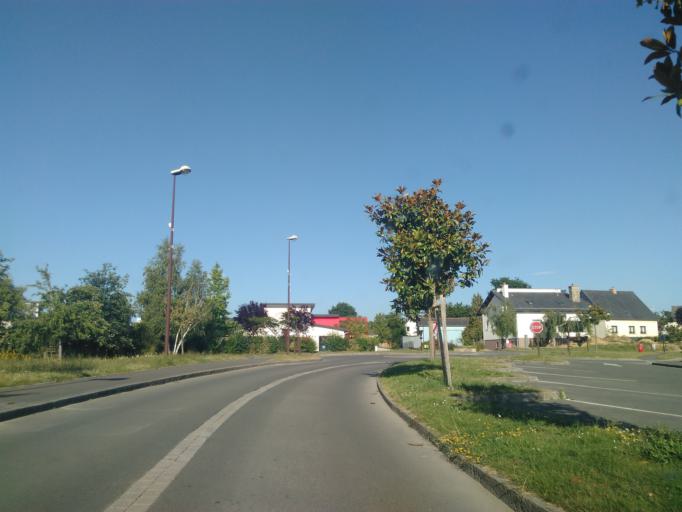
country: FR
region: Brittany
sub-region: Departement d'Ille-et-Vilaine
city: La Meziere
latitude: 48.2212
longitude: -1.7582
